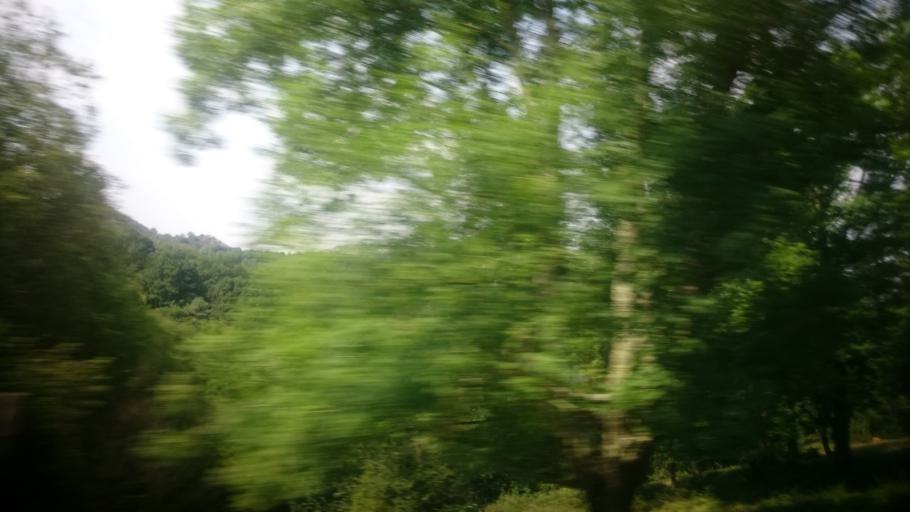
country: ES
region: Asturias
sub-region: Province of Asturias
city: Amieva
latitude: 43.3005
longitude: -5.0331
